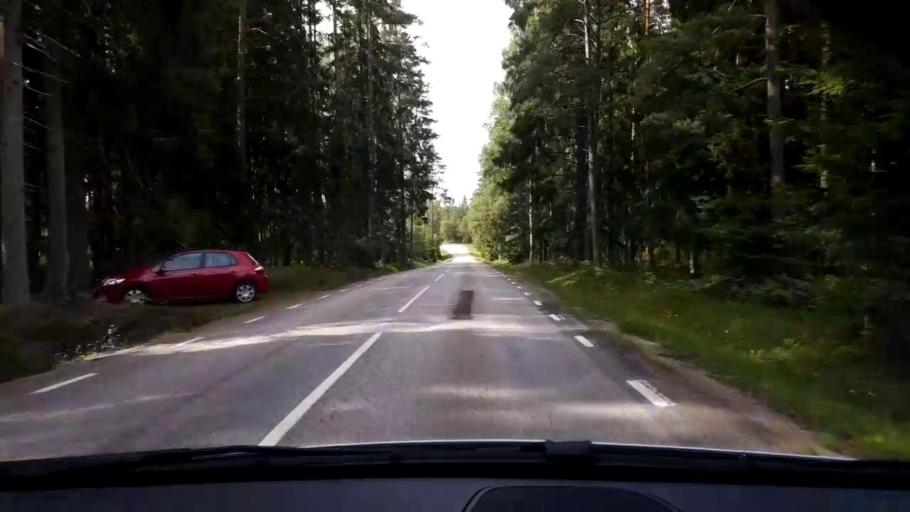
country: SE
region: Joenkoeping
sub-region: Vetlanda Kommun
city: Vetlanda
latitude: 57.3594
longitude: 15.0699
